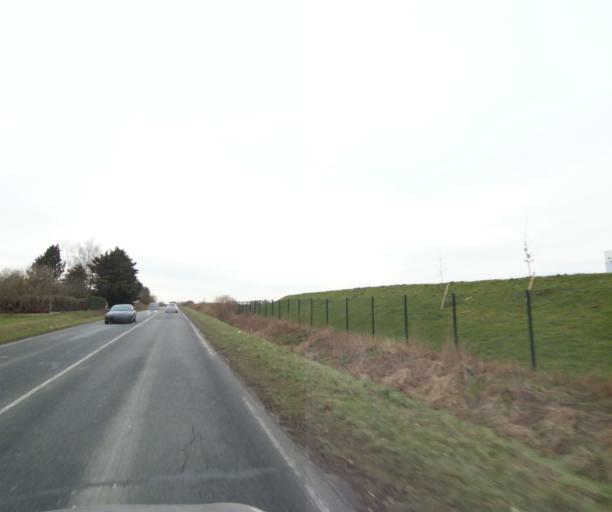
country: FR
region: Ile-de-France
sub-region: Departement de Seine-et-Marne
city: Dammartin-en-Goele
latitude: 49.0655
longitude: 2.6871
